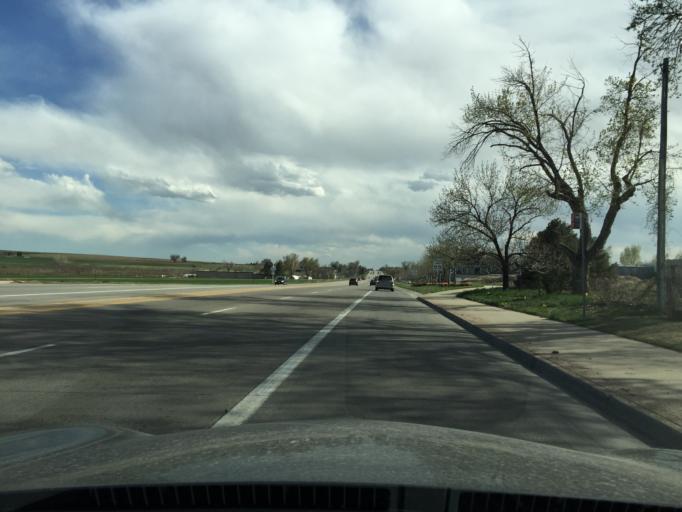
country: US
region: Colorado
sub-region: Boulder County
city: Longmont
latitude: 40.1381
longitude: -105.1025
